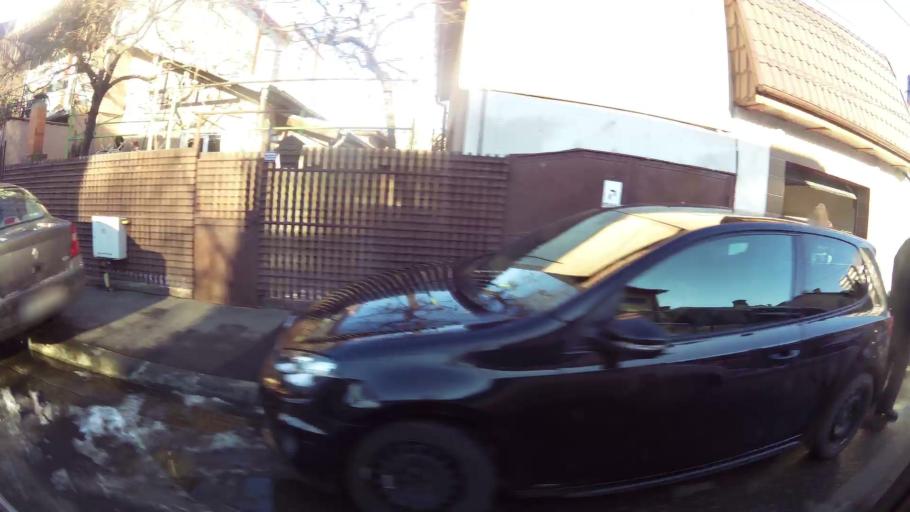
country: RO
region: Bucuresti
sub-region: Municipiul Bucuresti
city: Bucuresti
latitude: 44.3949
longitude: 26.0910
